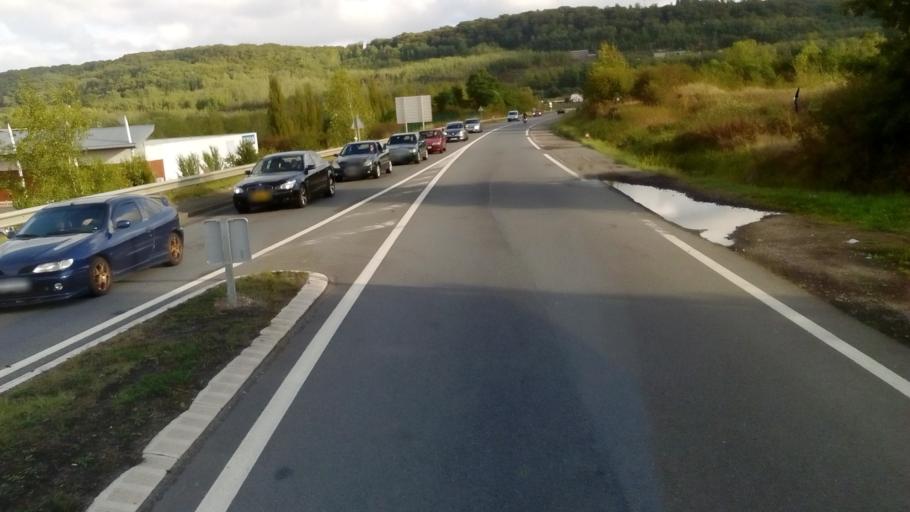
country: FR
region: Lorraine
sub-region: Departement de Meurthe-et-Moselle
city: Mont-Saint-Martin
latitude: 49.5451
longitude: 5.8037
